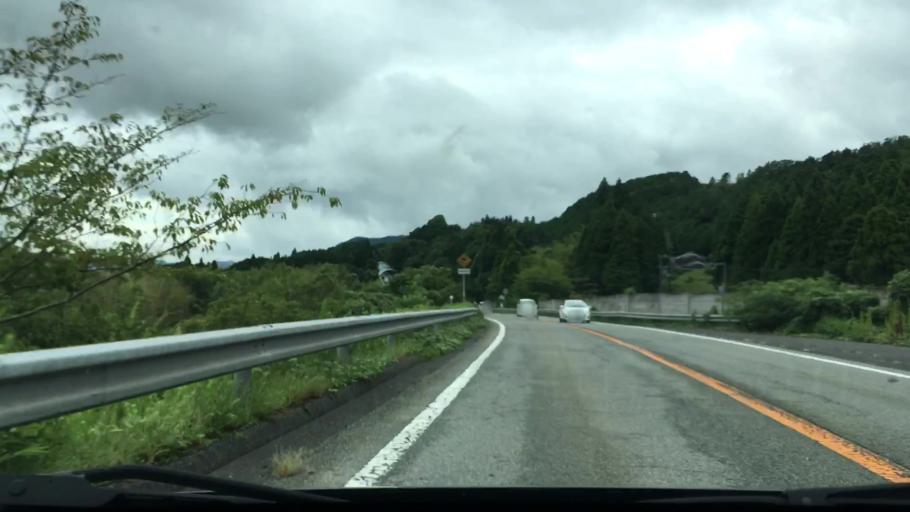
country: JP
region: Hyogo
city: Nishiwaki
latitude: 35.0838
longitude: 134.7752
